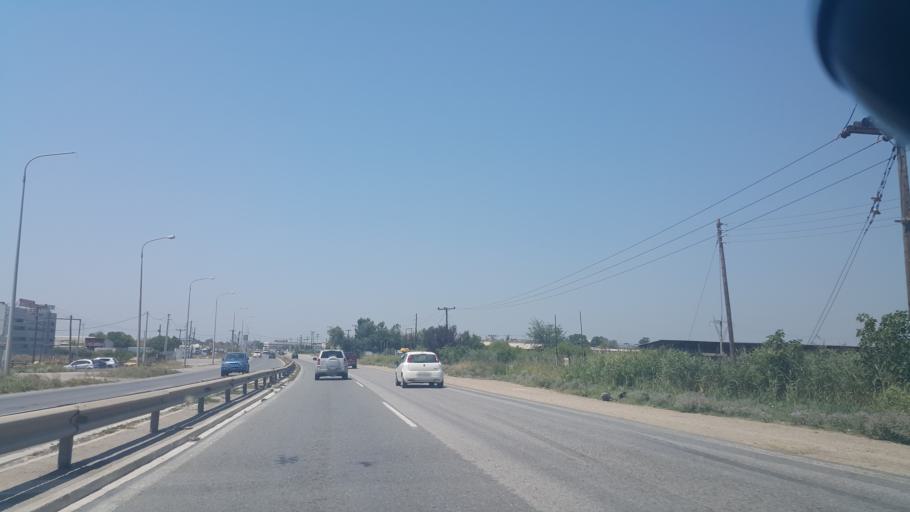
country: GR
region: Central Macedonia
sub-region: Nomos Thessalonikis
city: Sindos
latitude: 40.7056
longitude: 22.8068
